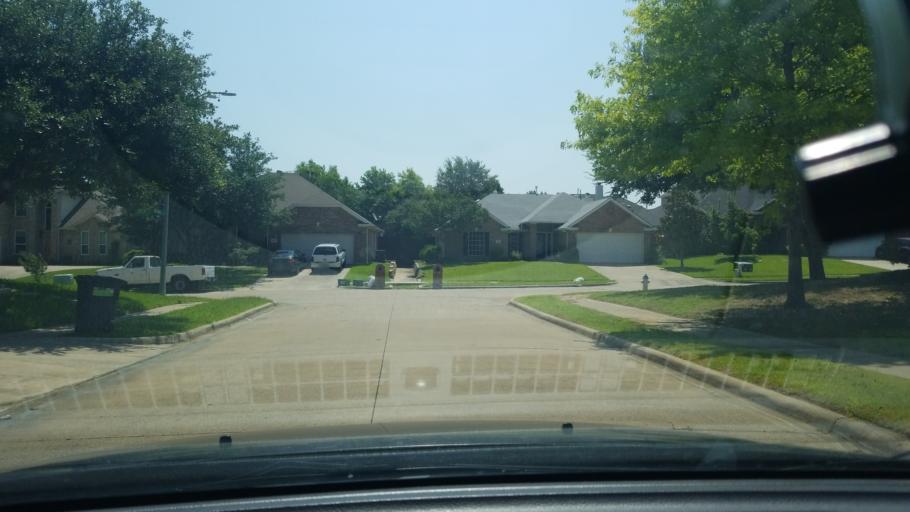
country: US
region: Texas
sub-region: Dallas County
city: Sunnyvale
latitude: 32.8274
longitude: -96.6006
